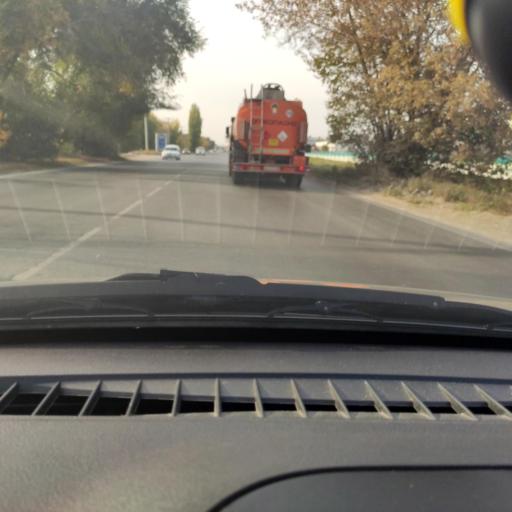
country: RU
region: Samara
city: Tol'yatti
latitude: 53.5321
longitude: 49.4588
